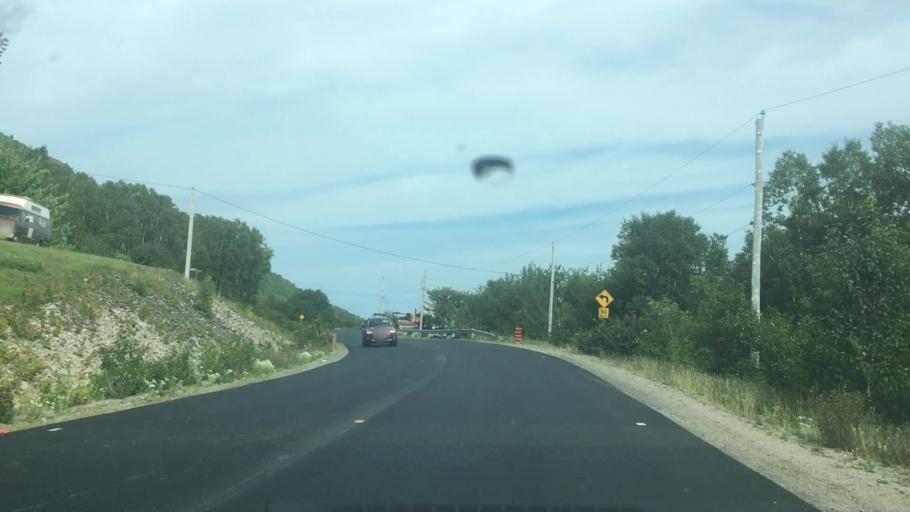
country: CA
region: Nova Scotia
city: Sydney Mines
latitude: 46.5762
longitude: -60.3905
